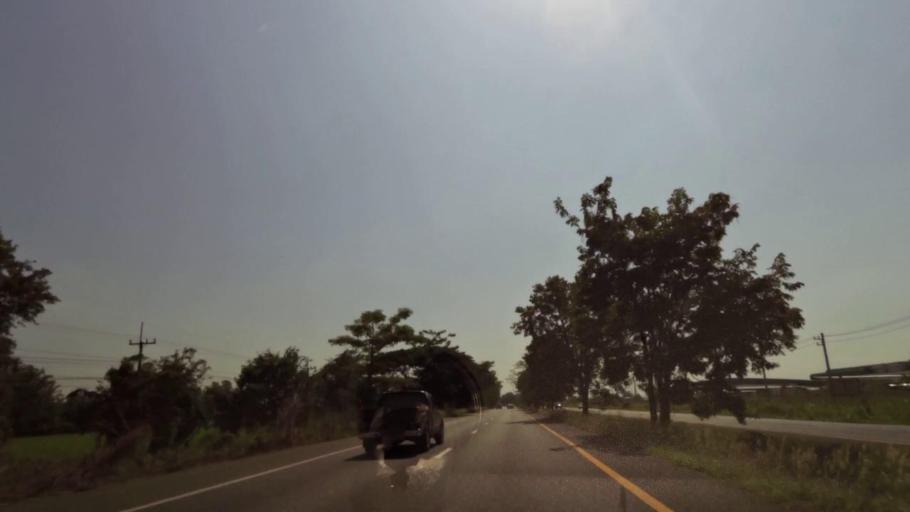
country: TH
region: Nakhon Sawan
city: Kao Liao
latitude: 15.9334
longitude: 100.1128
